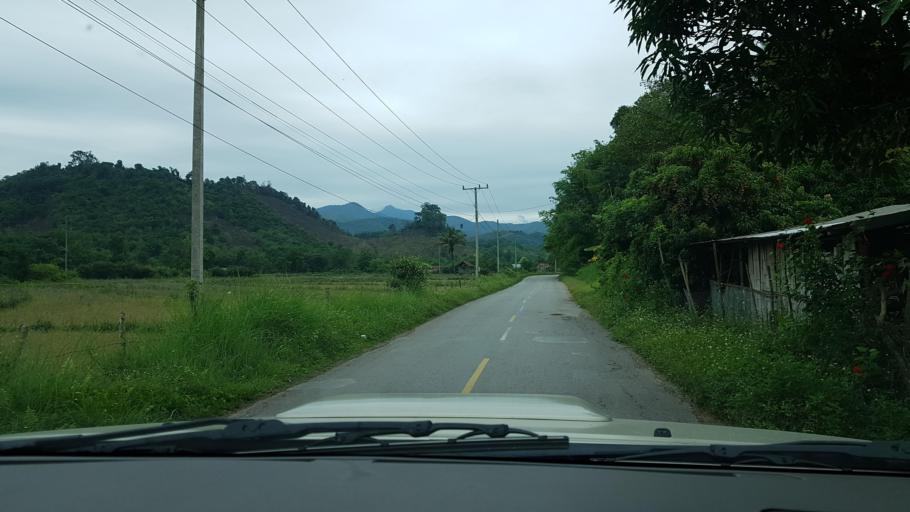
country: LA
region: Oudomxai
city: Muang La
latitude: 20.8442
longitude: 102.1050
